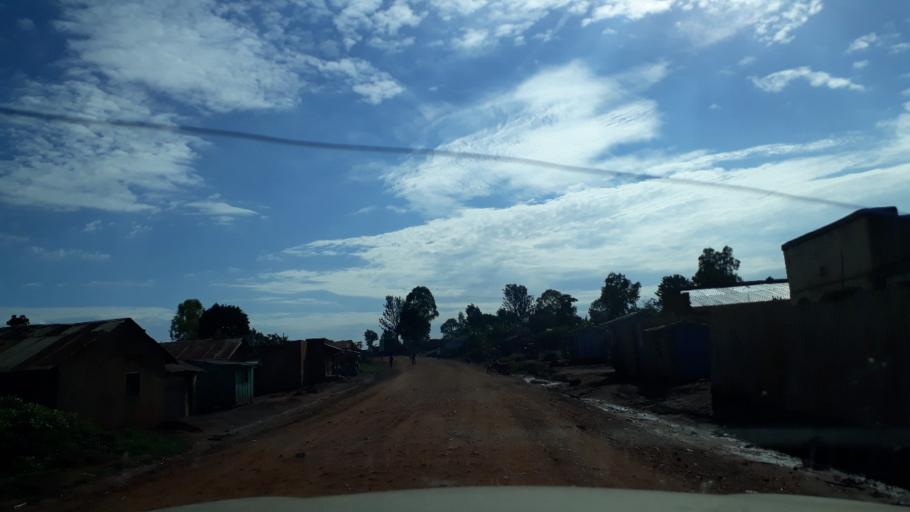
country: UG
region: Northern Region
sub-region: Zombo District
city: Paidha
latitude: 2.3086
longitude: 31.0223
